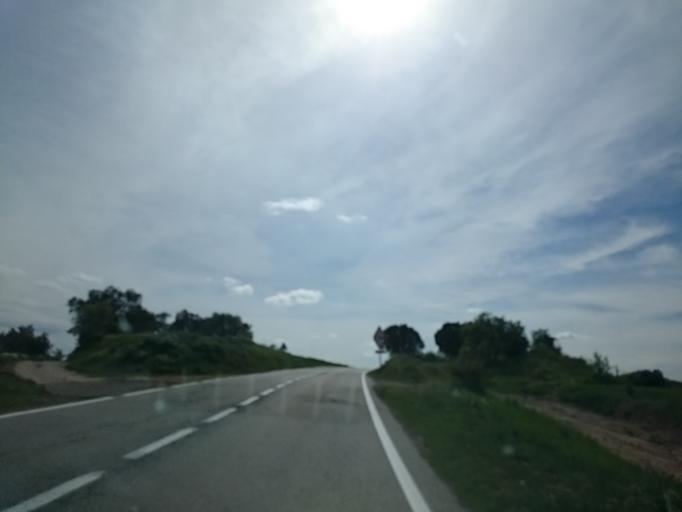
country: ES
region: Catalonia
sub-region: Provincia de Lleida
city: Sant Guim de Freixenet
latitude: 41.6570
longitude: 1.4299
